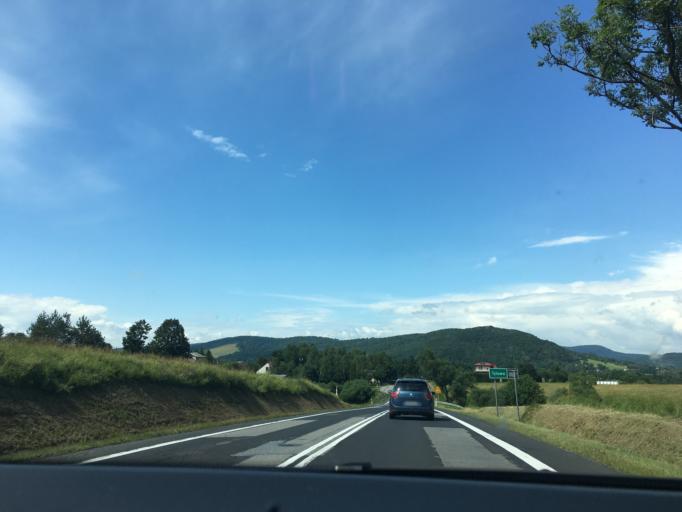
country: PL
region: Subcarpathian Voivodeship
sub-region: Powiat krosnienski
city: Dukla
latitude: 49.4519
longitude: 21.6931
